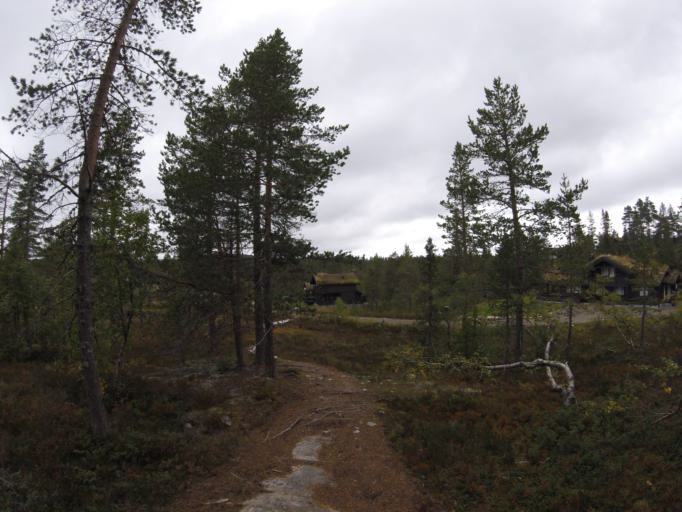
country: NO
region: Buskerud
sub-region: Flesberg
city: Lampeland
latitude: 59.7583
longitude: 9.3919
